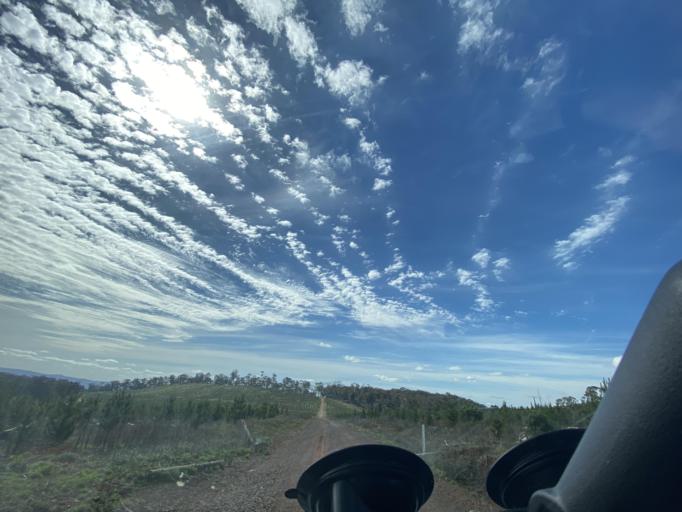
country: AU
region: Victoria
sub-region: Mansfield
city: Mansfield
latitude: -36.8233
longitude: 146.1034
